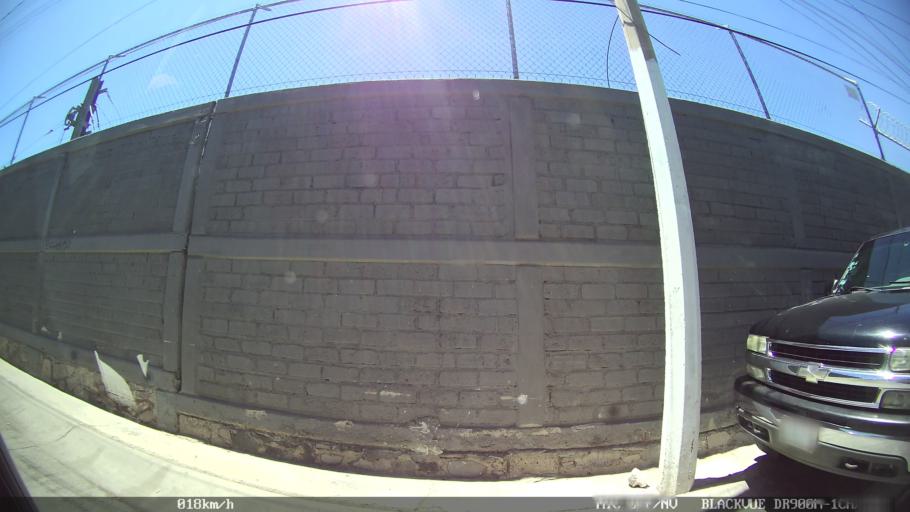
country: MX
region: Jalisco
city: Tlaquepaque
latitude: 20.6540
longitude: -103.2759
